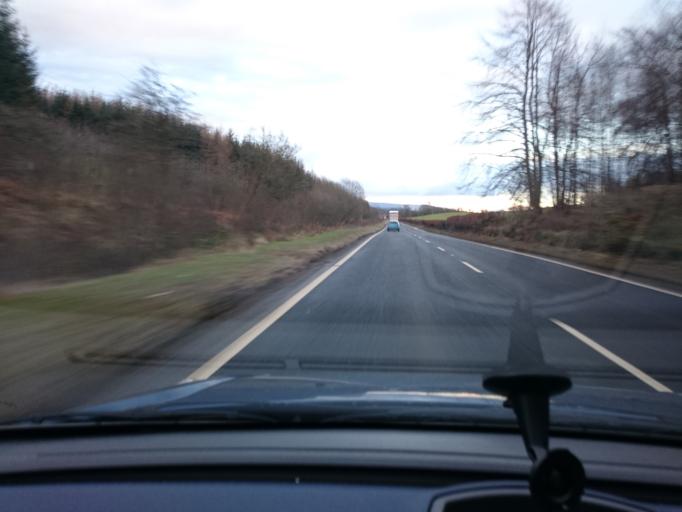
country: GB
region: Scotland
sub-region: Stirling
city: Doune
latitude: 56.2036
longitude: -4.0987
